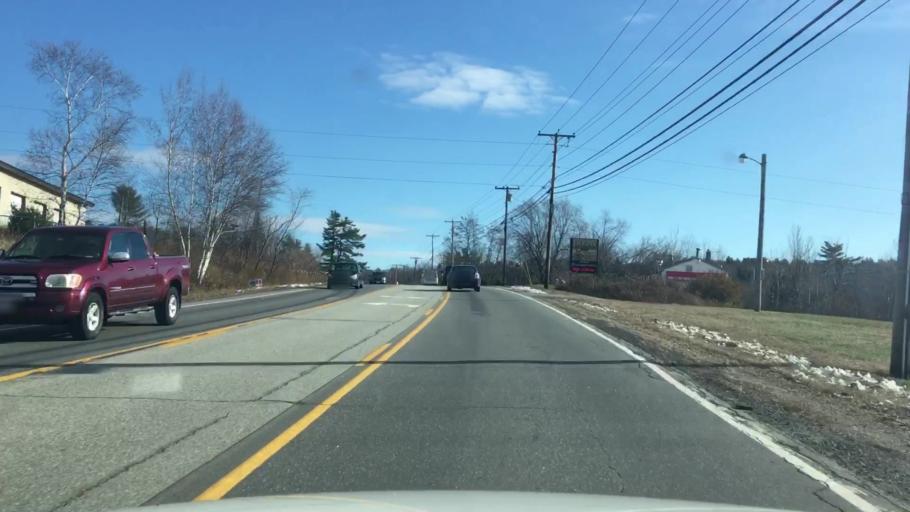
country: US
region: Maine
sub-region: Kennebec County
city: Manchester
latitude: 44.3214
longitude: -69.8430
